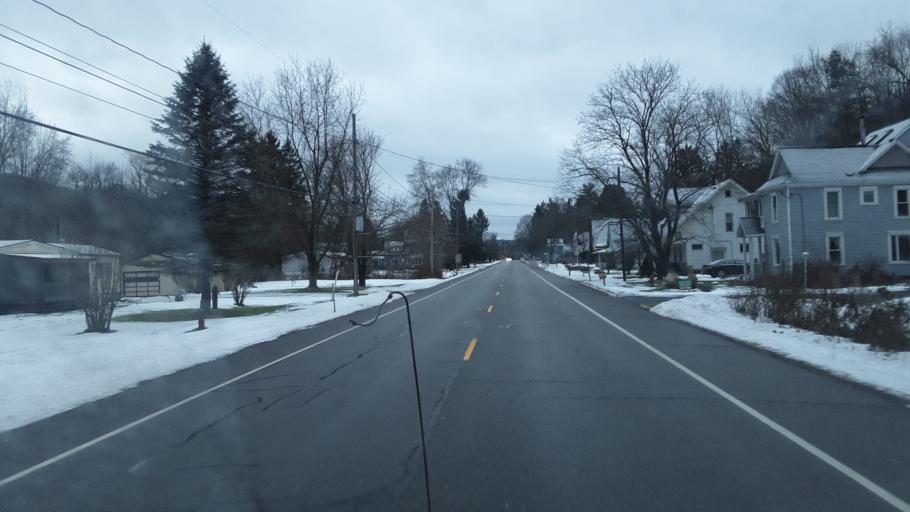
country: US
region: New York
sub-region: Steuben County
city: Hornell
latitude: 42.3291
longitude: -77.7321
